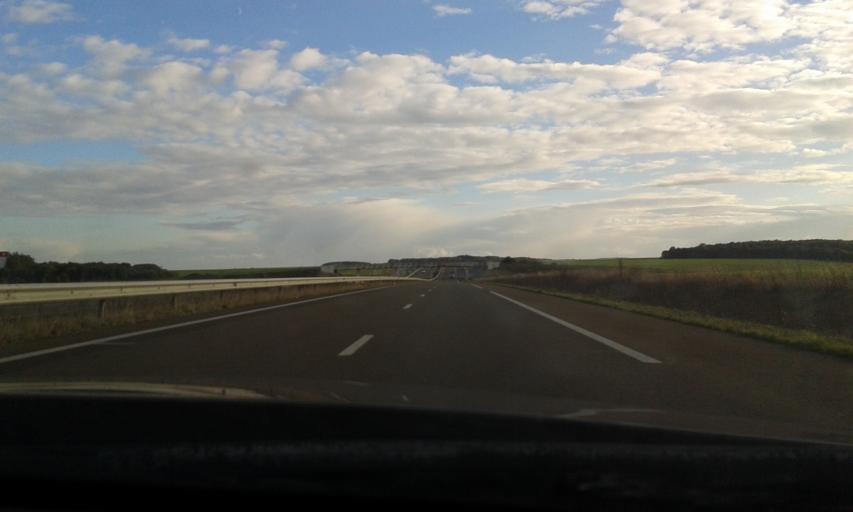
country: FR
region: Centre
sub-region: Departement d'Eure-et-Loir
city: Villemeux-sur-Eure
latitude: 48.6337
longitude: 1.4108
